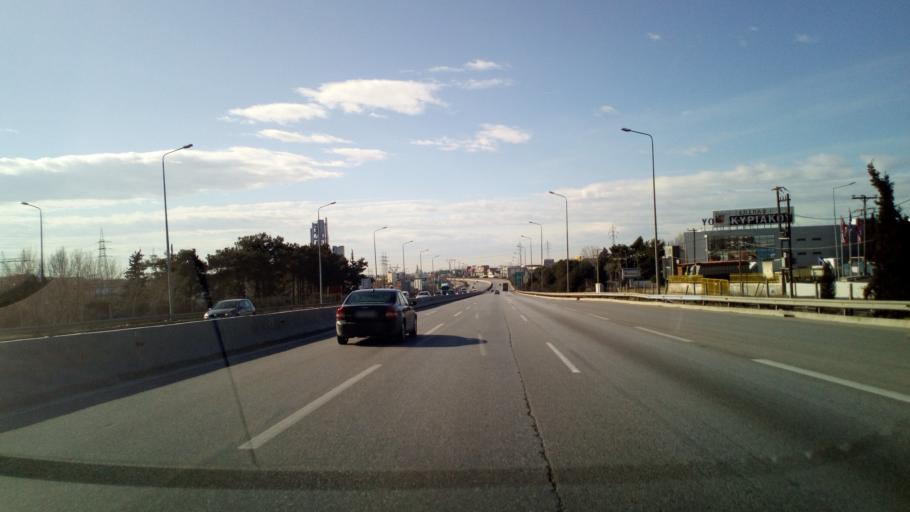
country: GR
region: Central Macedonia
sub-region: Nomos Thessalonikis
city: Efkarpia
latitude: 40.7104
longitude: 22.9568
